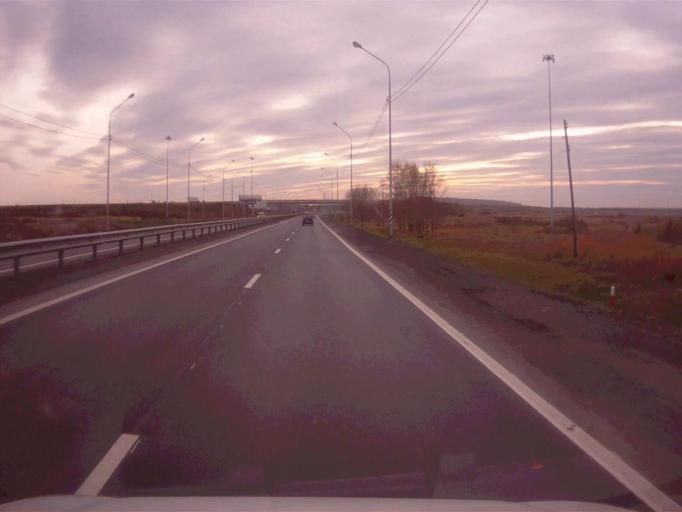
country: RU
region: Chelyabinsk
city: Roza
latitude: 54.9993
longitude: 61.4521
